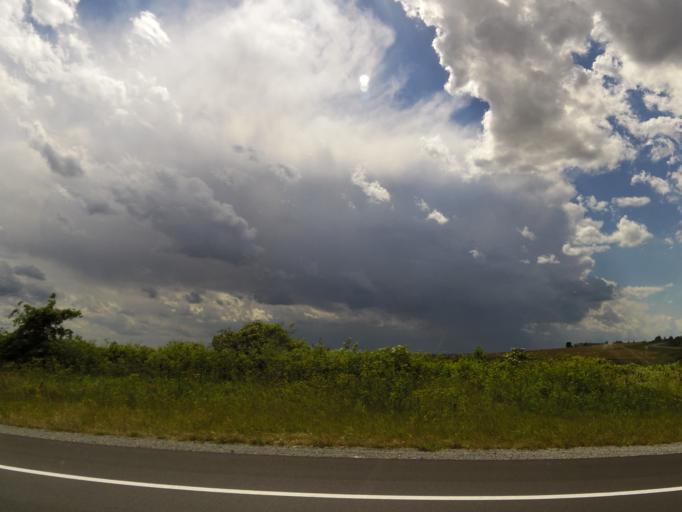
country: US
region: Iowa
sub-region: Johnson County
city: University Heights
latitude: 41.5971
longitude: -91.5477
